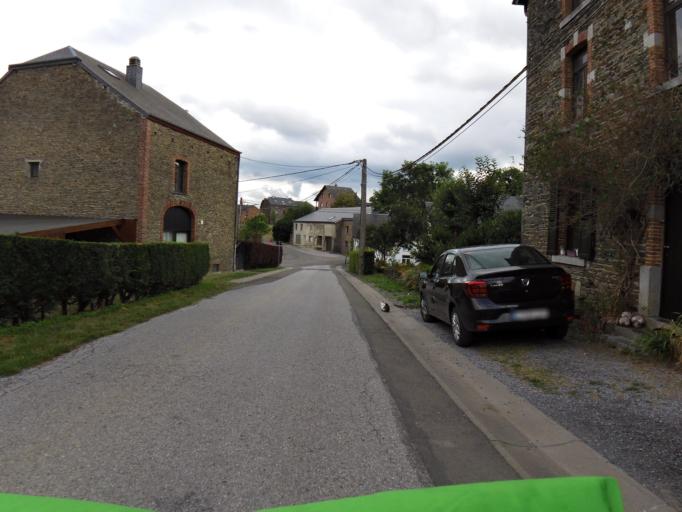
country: BE
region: Wallonia
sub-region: Province de Namur
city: Bievre
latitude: 49.9062
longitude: 4.9873
